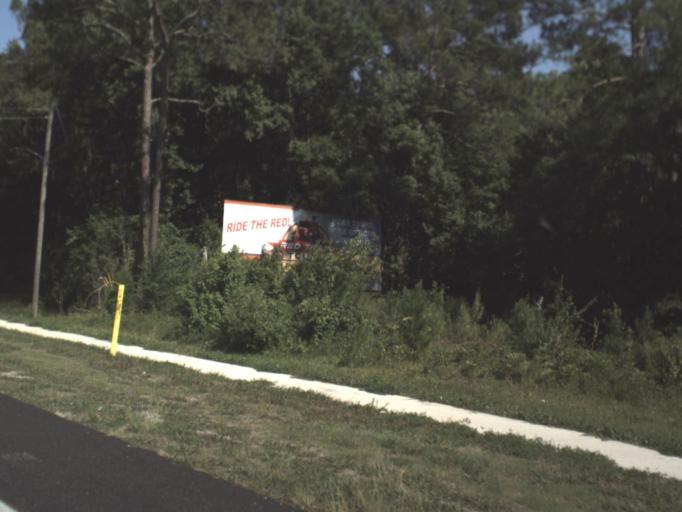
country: US
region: Florida
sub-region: Saint Johns County
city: Saint Augustine
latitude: 29.9136
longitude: -81.3933
